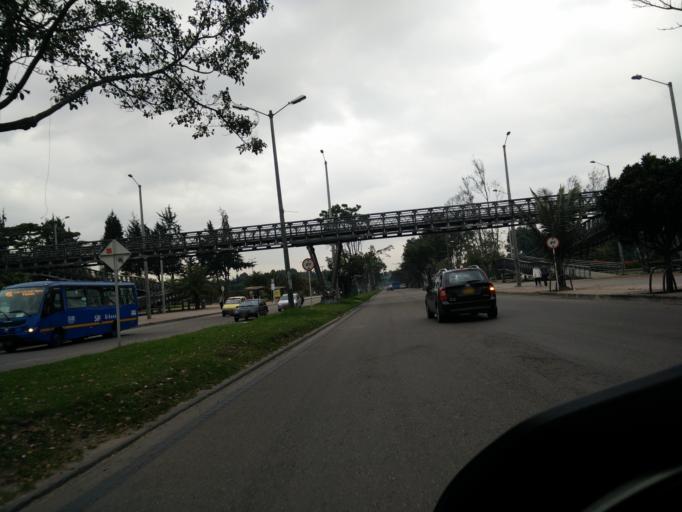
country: CO
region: Bogota D.C.
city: Bogota
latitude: 4.6602
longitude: -74.0891
